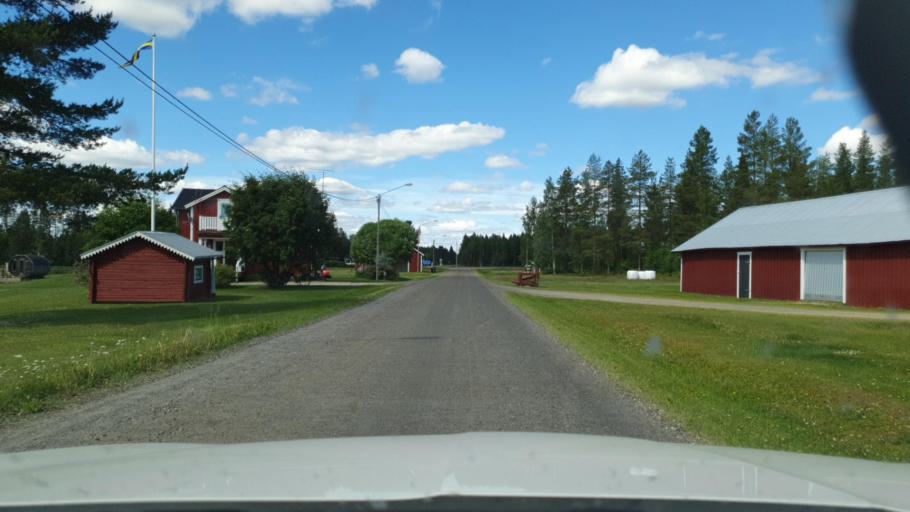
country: SE
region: Vaesterbotten
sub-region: Skelleftea Kommun
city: Backa
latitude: 65.1841
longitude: 21.0649
